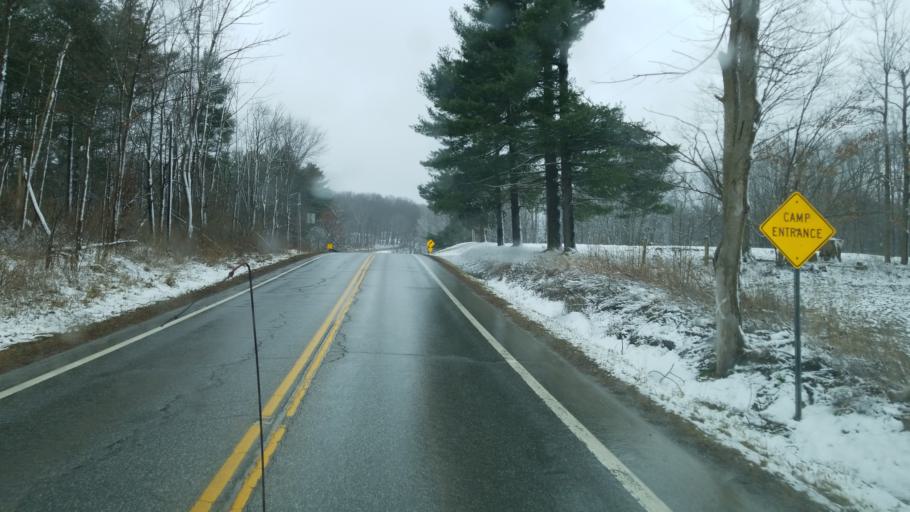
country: US
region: Ohio
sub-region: Geauga County
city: Middlefield
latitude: 41.3831
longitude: -81.0771
